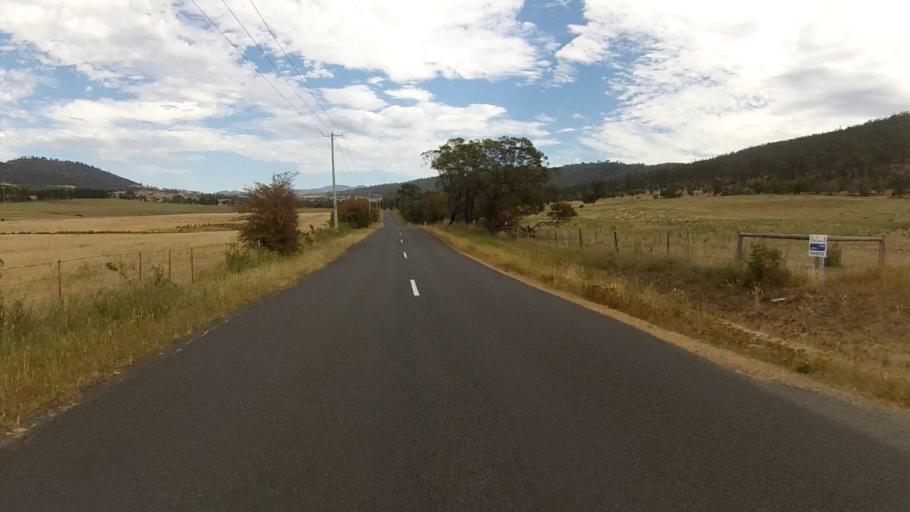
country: AU
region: Tasmania
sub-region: Clarence
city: Cambridge
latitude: -42.7276
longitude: 147.3994
